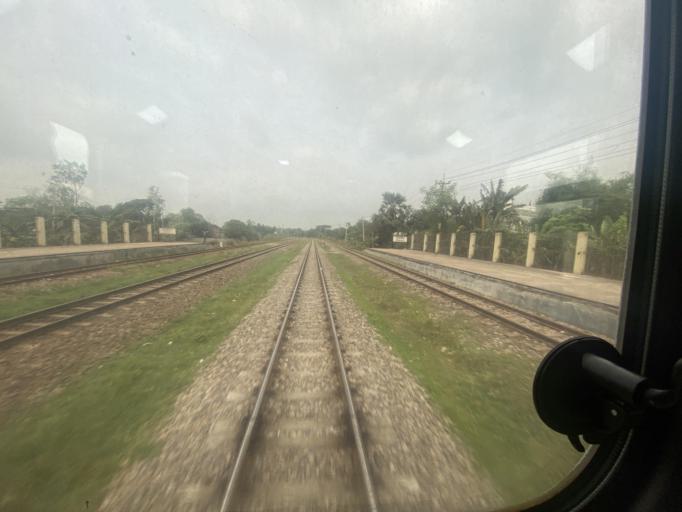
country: BD
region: Dhaka
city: Tungi
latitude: 23.9364
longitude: 90.4758
